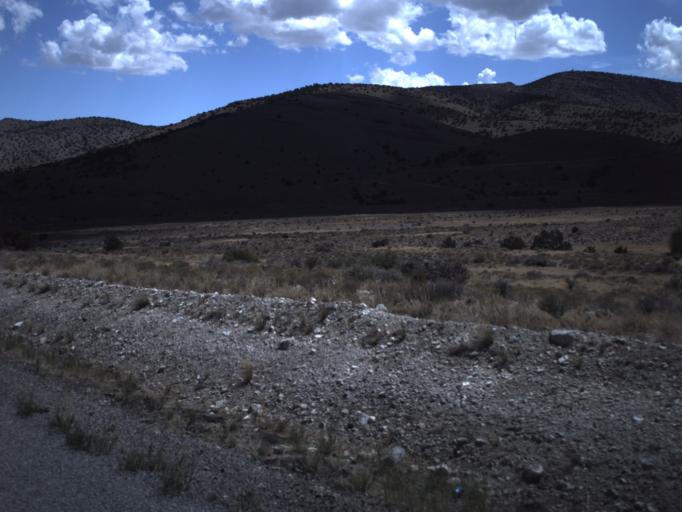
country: US
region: Utah
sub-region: Beaver County
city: Milford
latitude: 39.0780
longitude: -113.6162
